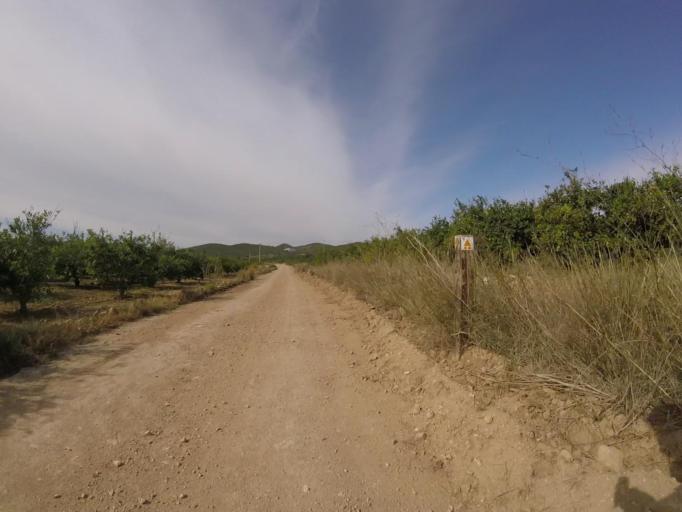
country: ES
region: Valencia
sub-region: Provincia de Castello
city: Torreblanca
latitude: 40.1969
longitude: 0.1621
